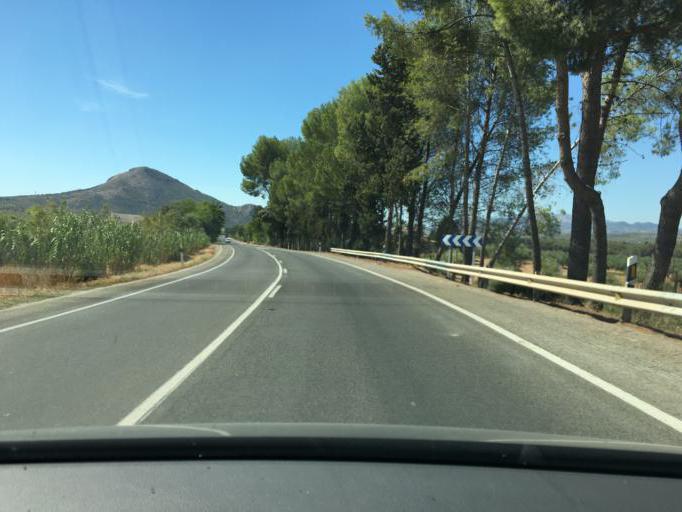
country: ES
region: Andalusia
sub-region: Provincia de Granada
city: Albolote
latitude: 37.2679
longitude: -3.6670
